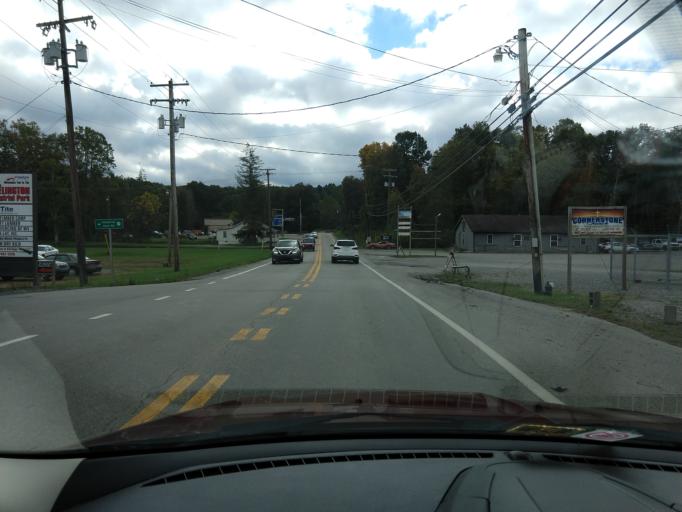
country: US
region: West Virginia
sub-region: Barbour County
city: Belington
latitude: 39.0131
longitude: -79.9388
